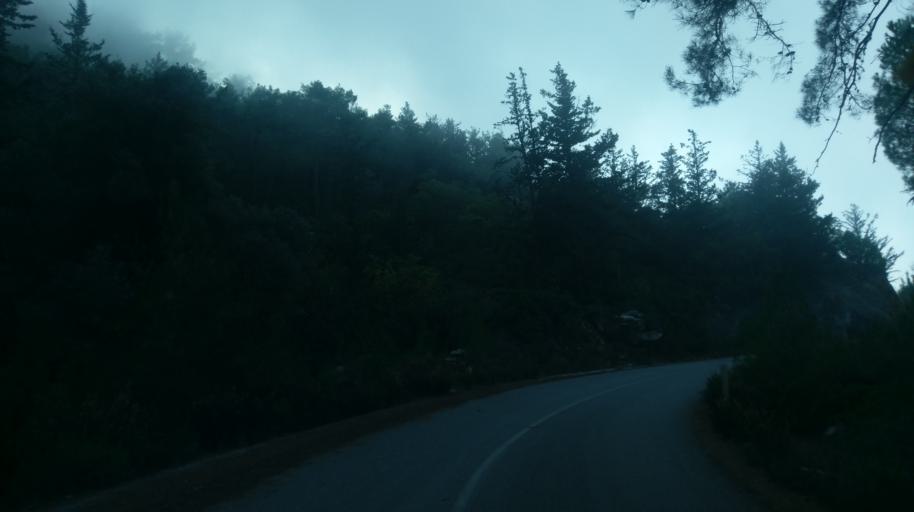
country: CY
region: Ammochostos
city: Trikomo
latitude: 35.3817
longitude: 33.8694
